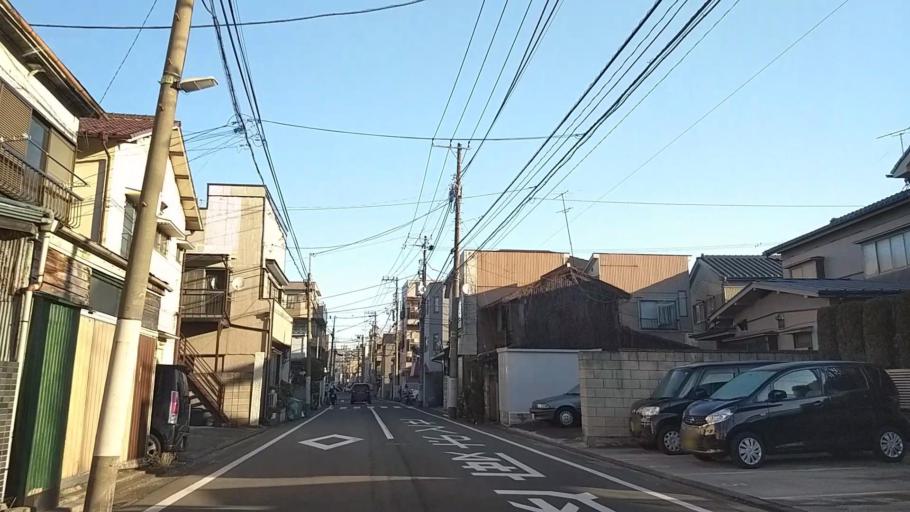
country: JP
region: Kanagawa
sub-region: Kawasaki-shi
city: Kawasaki
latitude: 35.4960
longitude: 139.6742
